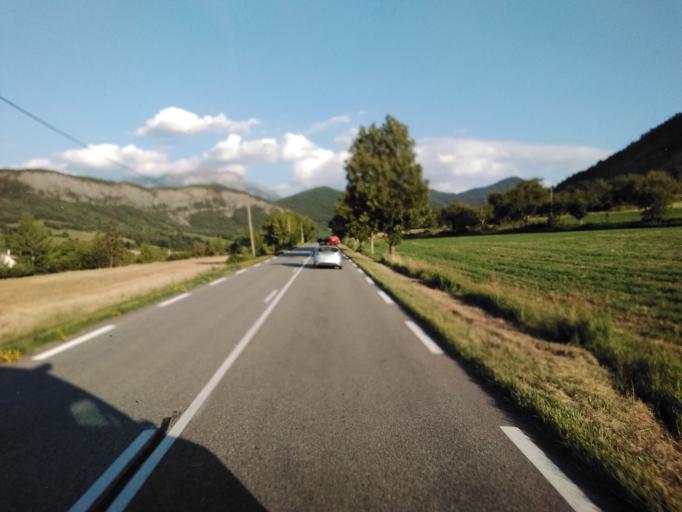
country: FR
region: Provence-Alpes-Cote d'Azur
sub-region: Departement des Hautes-Alpes
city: Chorges
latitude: 44.4561
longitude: 6.2925
